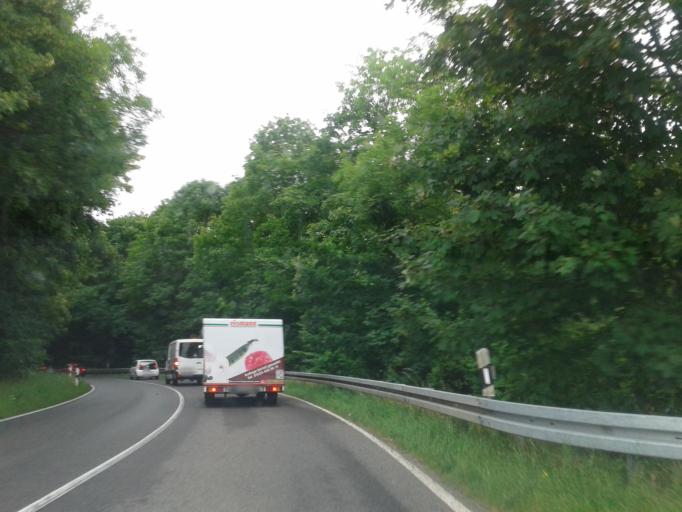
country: DE
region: Saxony
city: Tharandt
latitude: 50.9781
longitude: 13.5678
